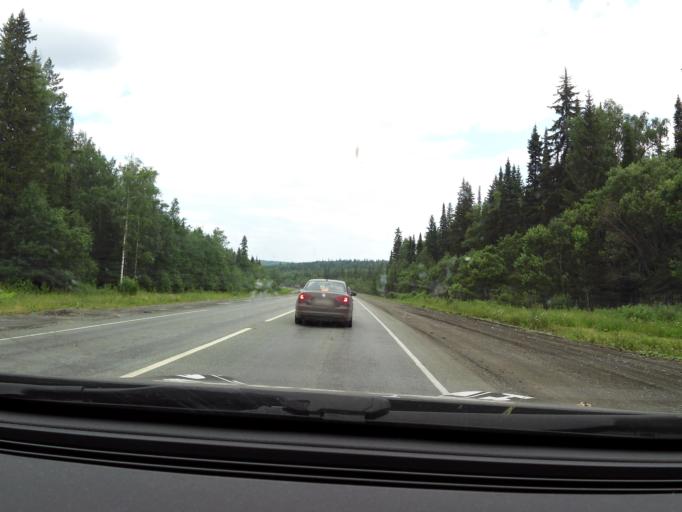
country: RU
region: Sverdlovsk
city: Bilimbay
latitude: 56.8543
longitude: 59.7728
